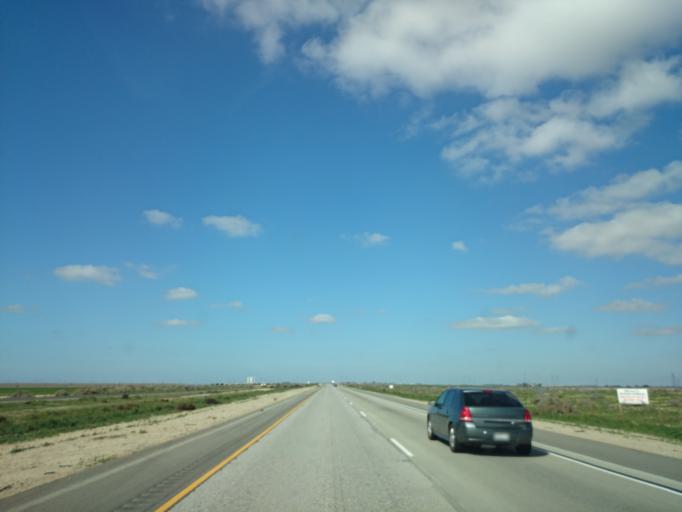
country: US
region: California
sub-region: Kern County
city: Buttonwillow
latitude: 35.3664
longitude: -119.3519
